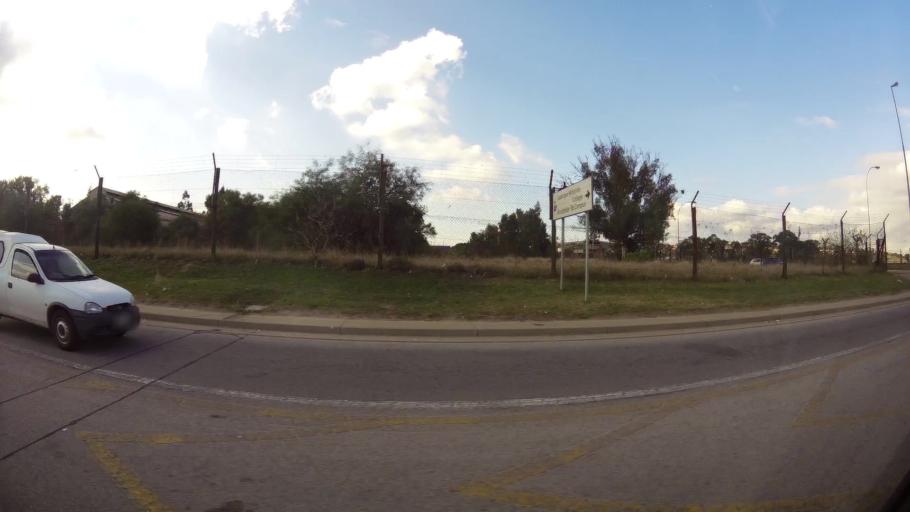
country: ZA
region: Eastern Cape
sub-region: Nelson Mandela Bay Metropolitan Municipality
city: Uitenhage
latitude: -33.7748
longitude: 25.4041
